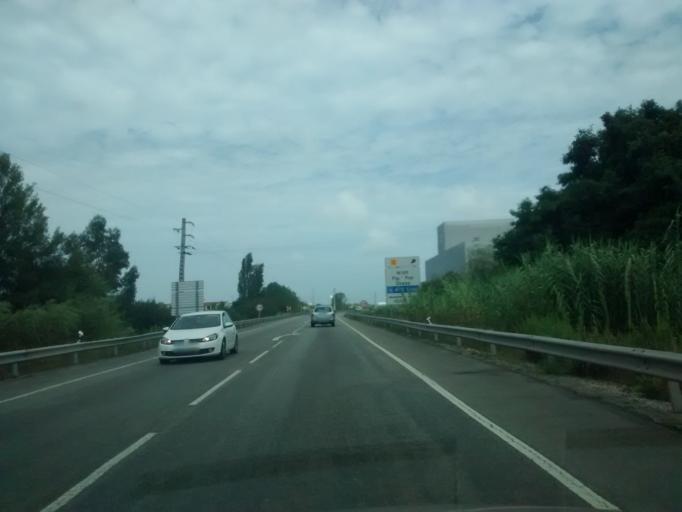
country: PT
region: Aveiro
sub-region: Aveiro
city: Aradas
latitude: 40.6176
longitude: -8.6393
